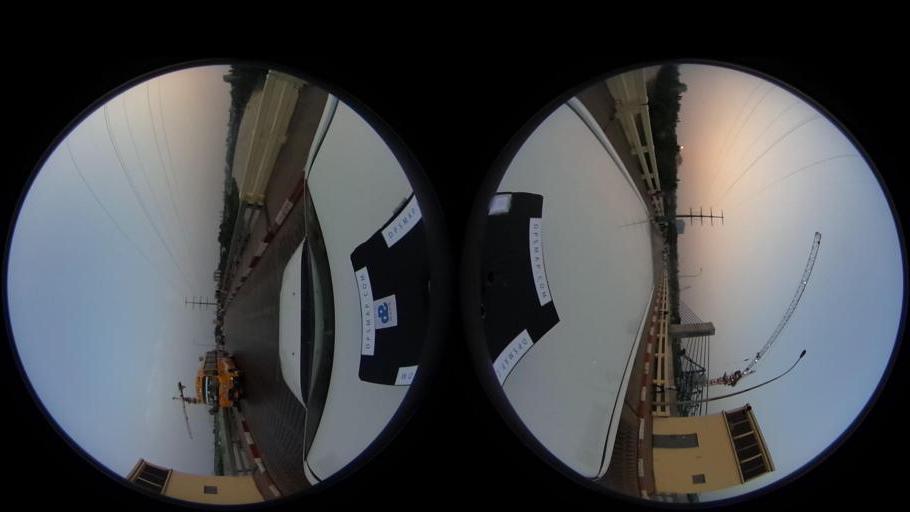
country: MM
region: Yangon
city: Yangon
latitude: 16.7853
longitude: 96.1790
